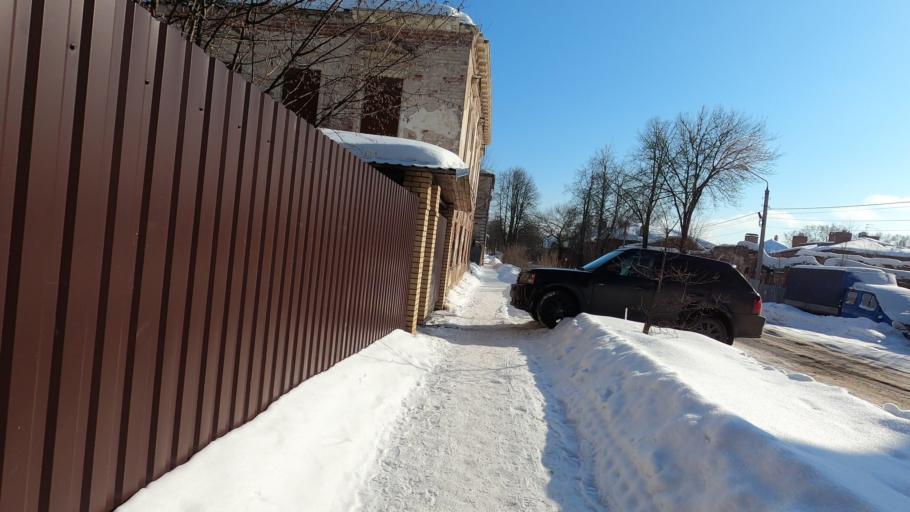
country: RU
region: Jaroslavl
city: Rybinsk
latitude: 58.0468
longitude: 38.8628
